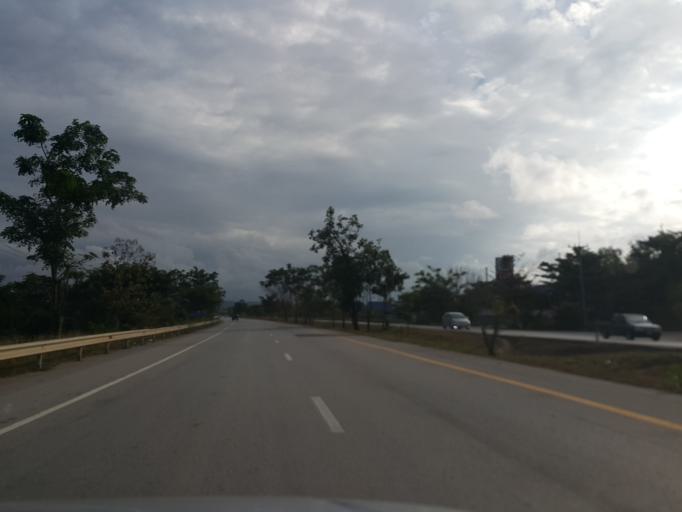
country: TH
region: Lampang
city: Ko Kha
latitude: 18.1590
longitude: 99.4037
